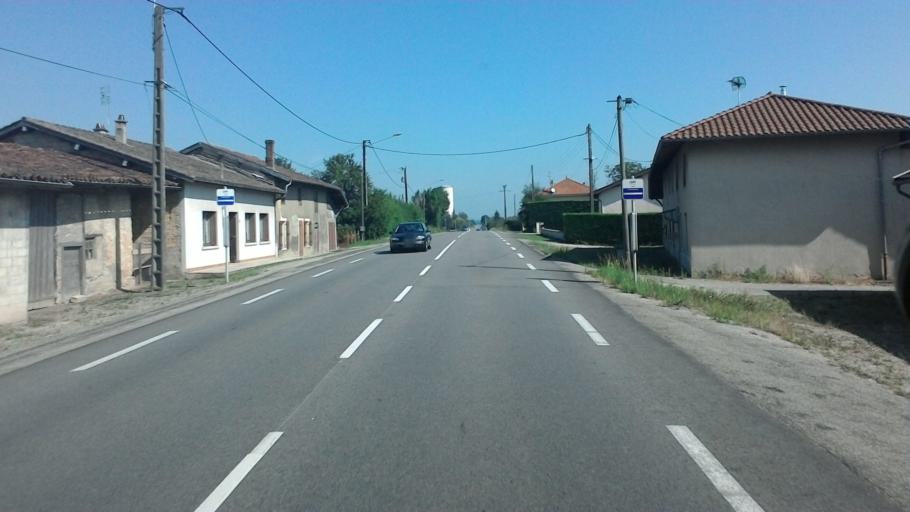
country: FR
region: Rhone-Alpes
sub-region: Departement de l'Ain
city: Montrevel-en-Bresse
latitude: 46.3607
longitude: 5.1227
